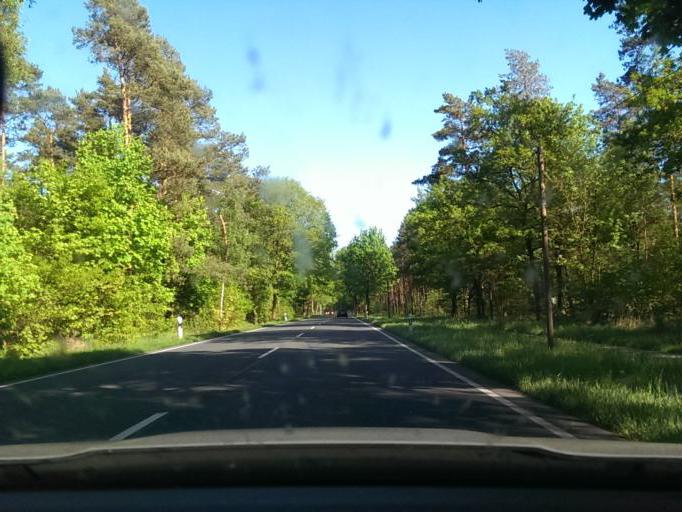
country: DE
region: Lower Saxony
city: Wietze
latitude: 52.6398
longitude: 9.8828
